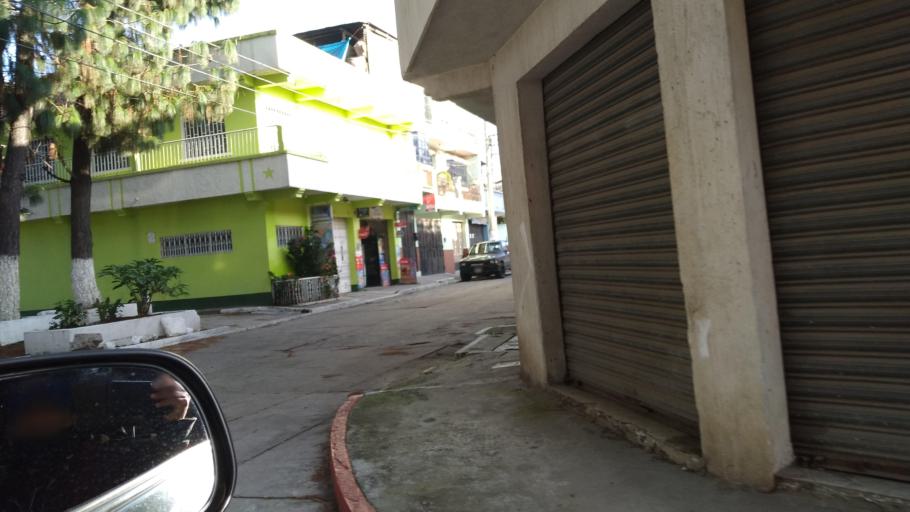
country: GT
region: Quetzaltenango
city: Quetzaltenango
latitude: 14.8517
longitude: -91.5215
